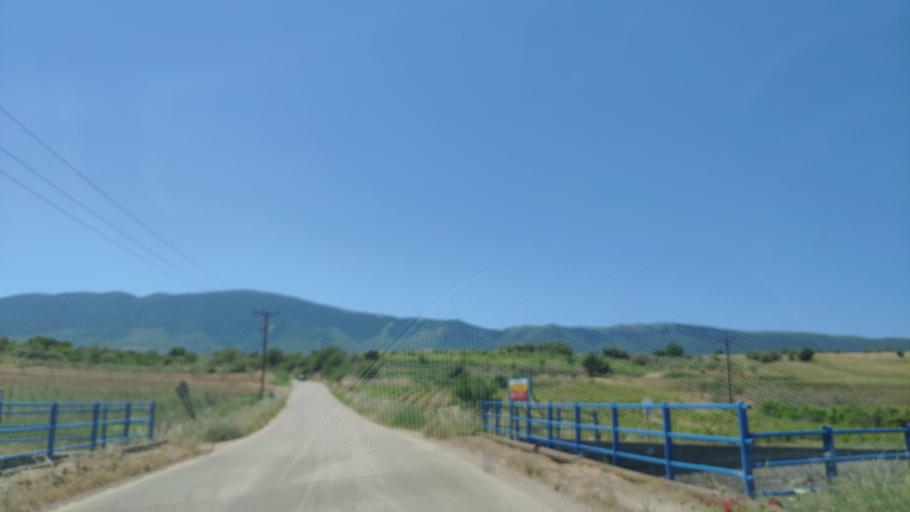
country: GR
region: Central Greece
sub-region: Nomos Voiotias
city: Kaparellion
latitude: 38.2515
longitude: 23.2352
